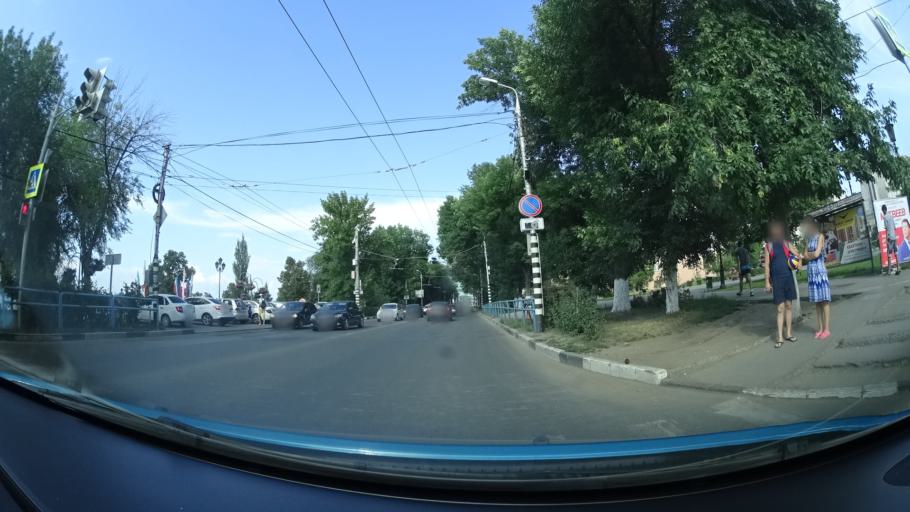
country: RU
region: Samara
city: Samara
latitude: 53.2092
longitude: 50.1183
